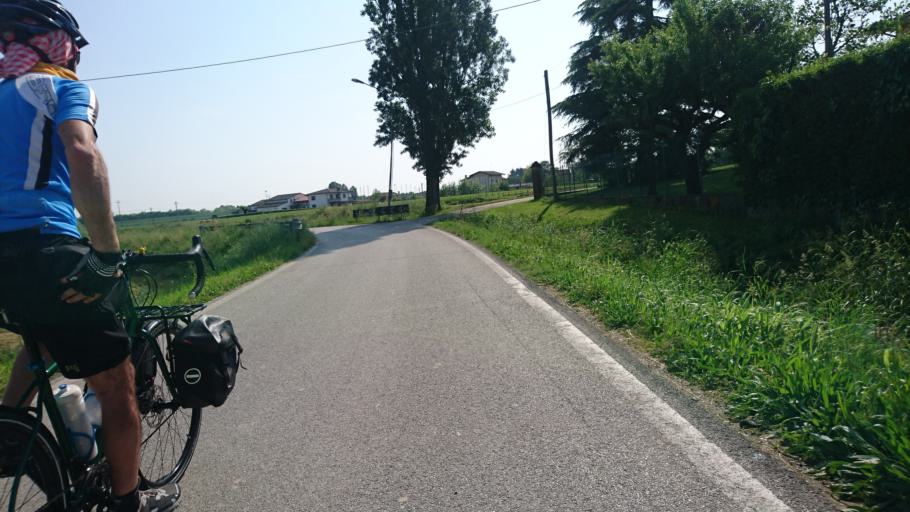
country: IT
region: Veneto
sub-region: Provincia di Venezia
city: Galta
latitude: 45.3682
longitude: 12.0220
